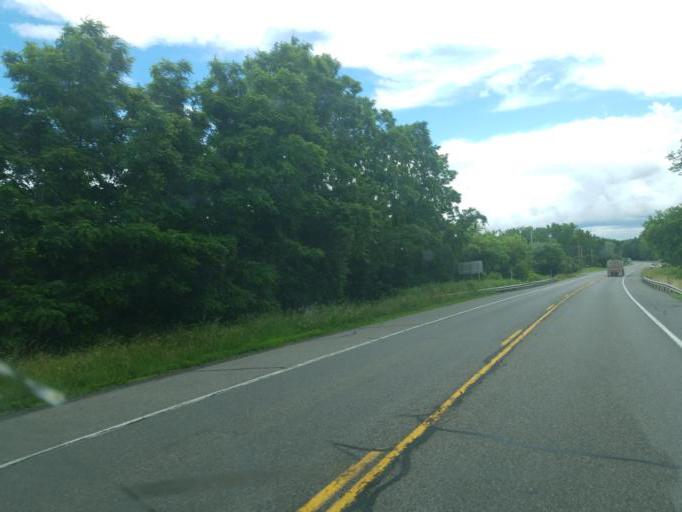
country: US
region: New York
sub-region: Ontario County
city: Phelps
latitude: 42.9561
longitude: -76.9776
